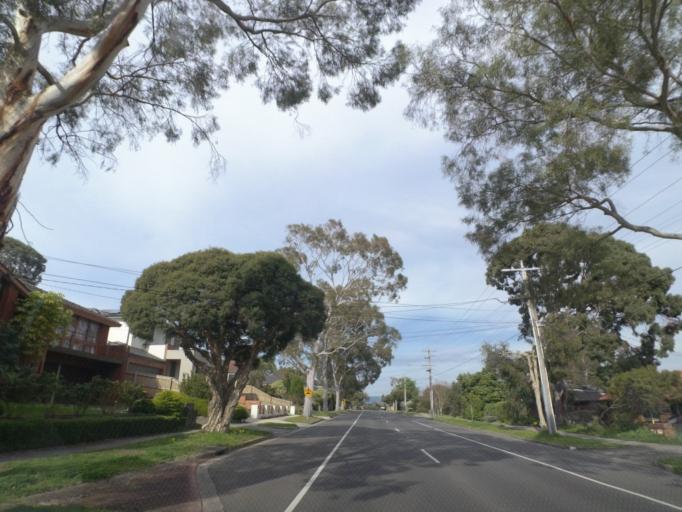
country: AU
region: Victoria
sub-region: Whitehorse
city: Vermont
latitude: -37.8503
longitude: 145.1974
